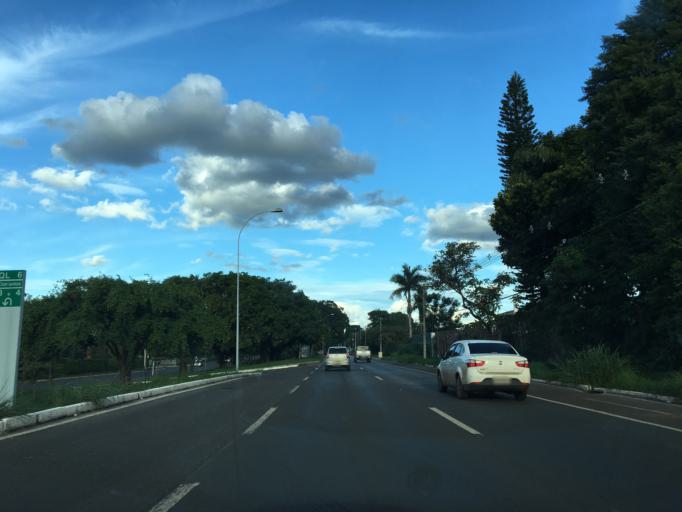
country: BR
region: Federal District
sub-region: Brasilia
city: Brasilia
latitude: -15.8493
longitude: -47.9064
